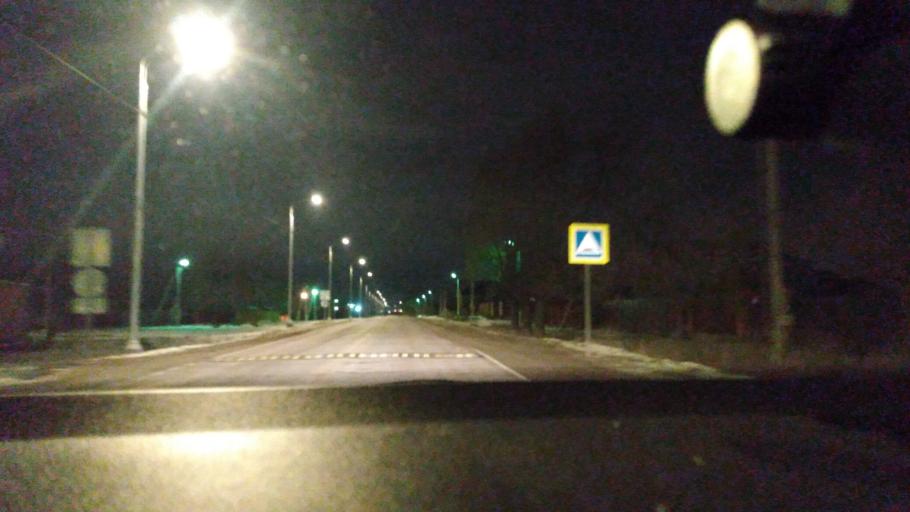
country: RU
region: Moskovskaya
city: Lukhovitsy
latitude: 55.0911
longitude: 38.9466
